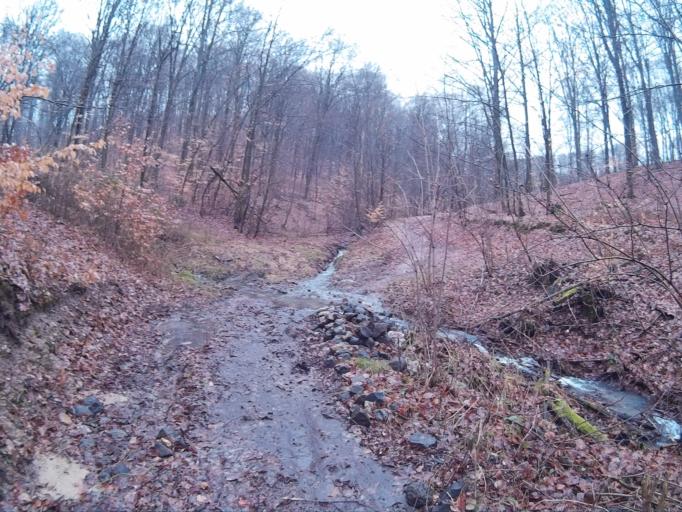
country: HU
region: Borsod-Abauj-Zemplen
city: Sarospatak
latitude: 48.4206
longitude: 21.5529
